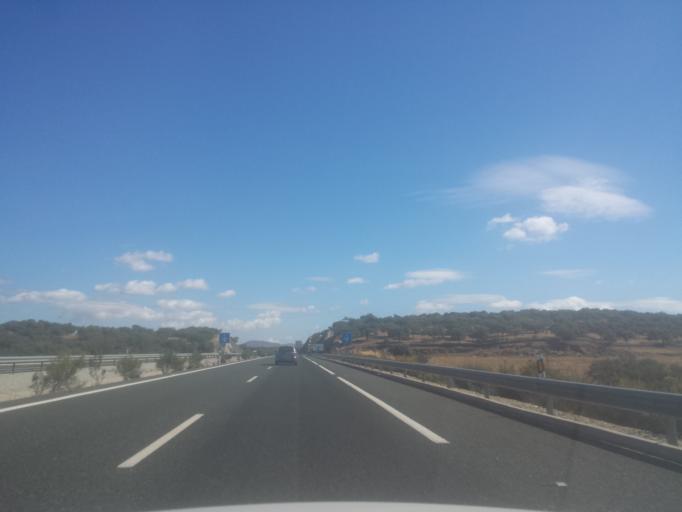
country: ES
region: Andalusia
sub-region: Provincia de Huelva
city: Santa Olalla del Cala
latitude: 37.8971
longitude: -6.2151
